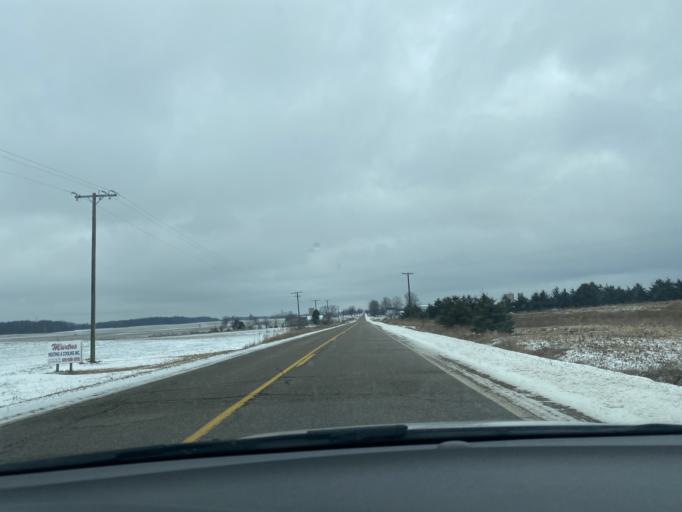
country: US
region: Michigan
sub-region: Lapeer County
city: North Branch
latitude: 43.2099
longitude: -83.1159
